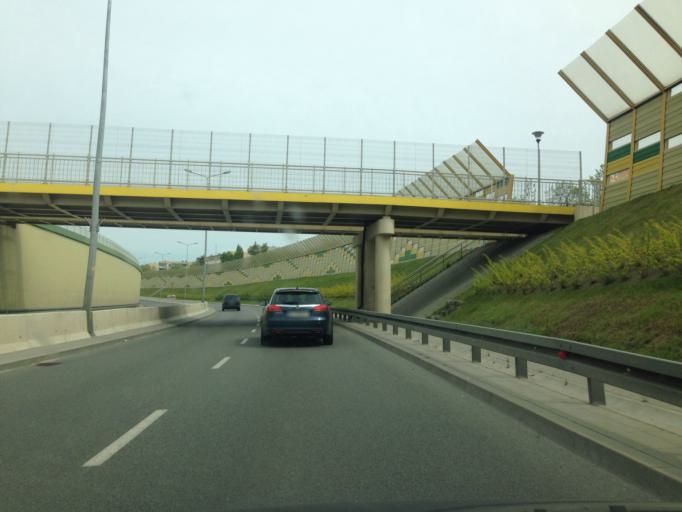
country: PL
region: Pomeranian Voivodeship
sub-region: Sopot
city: Sopot
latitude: 54.4233
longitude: 18.5706
